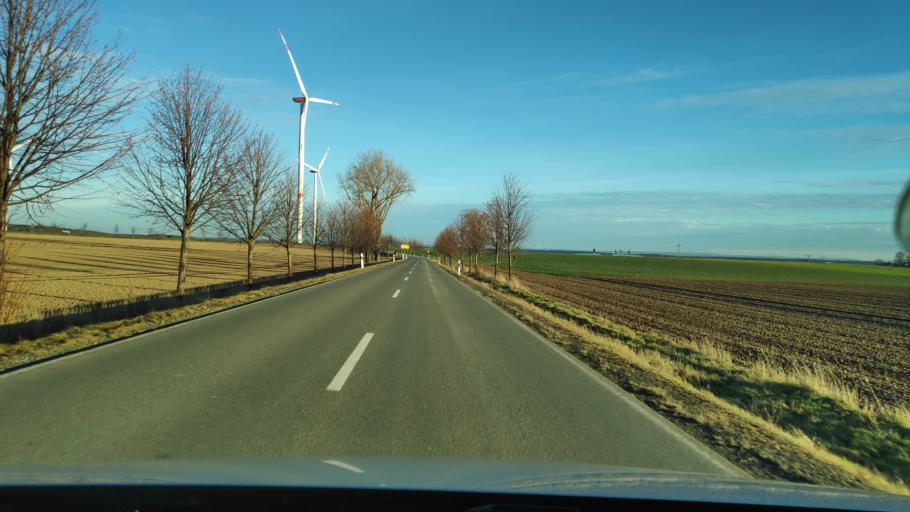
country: DE
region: Thuringia
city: Thonhausen
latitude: 50.8234
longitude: 12.3311
